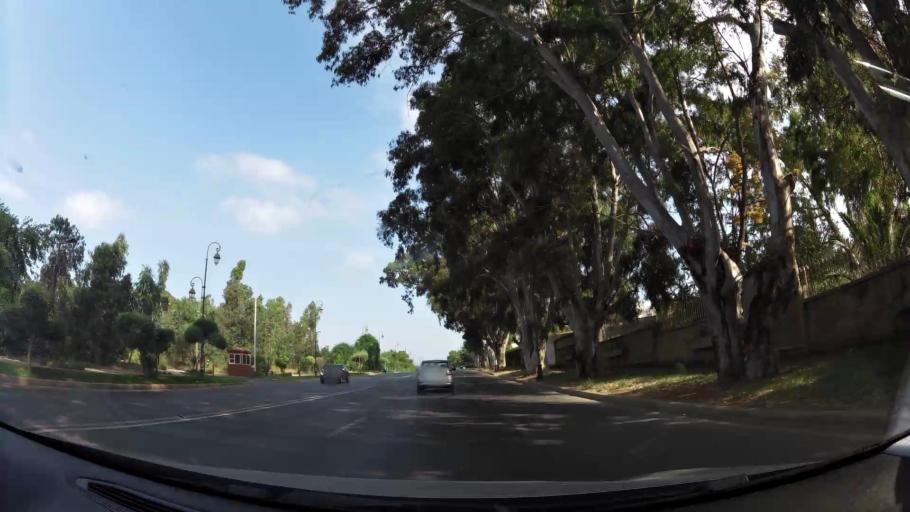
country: MA
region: Rabat-Sale-Zemmour-Zaer
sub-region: Rabat
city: Rabat
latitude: 33.9558
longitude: -6.8169
